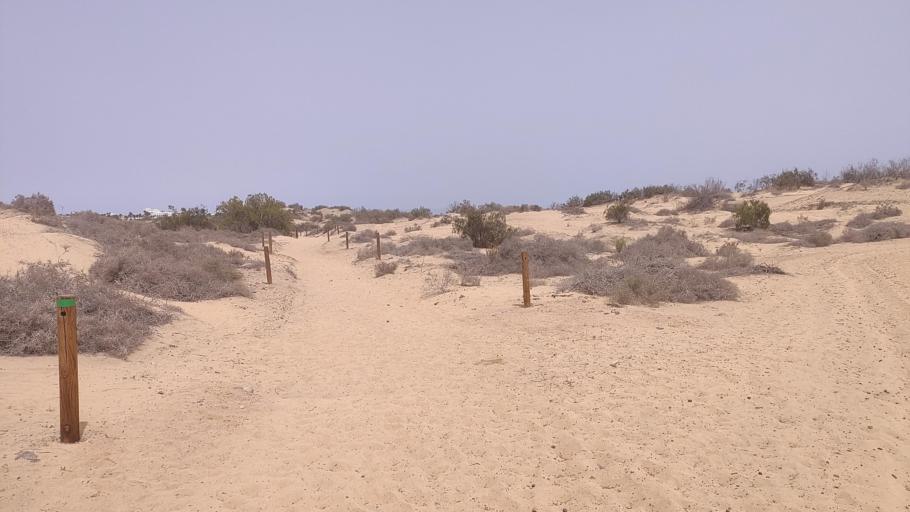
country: ES
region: Canary Islands
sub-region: Provincia de Las Palmas
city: Maspalomas
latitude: 27.7453
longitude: -15.5910
